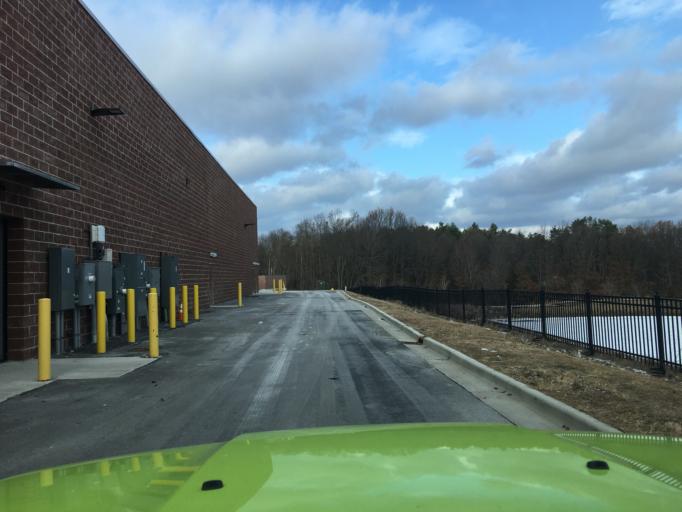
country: US
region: Michigan
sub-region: Kent County
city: Northview
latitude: 43.0021
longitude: -85.5878
